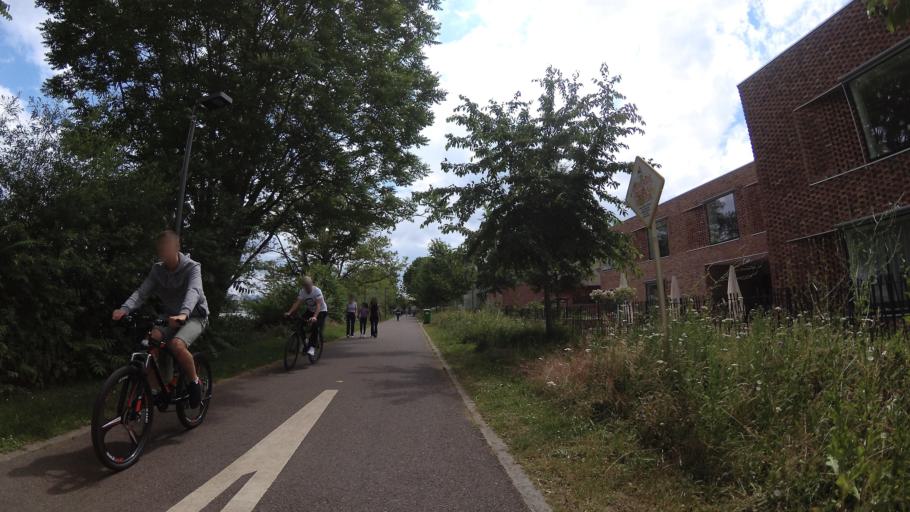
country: FR
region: Alsace
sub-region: Departement du Haut-Rhin
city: Village-Neuf
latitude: 47.5887
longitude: 7.5867
